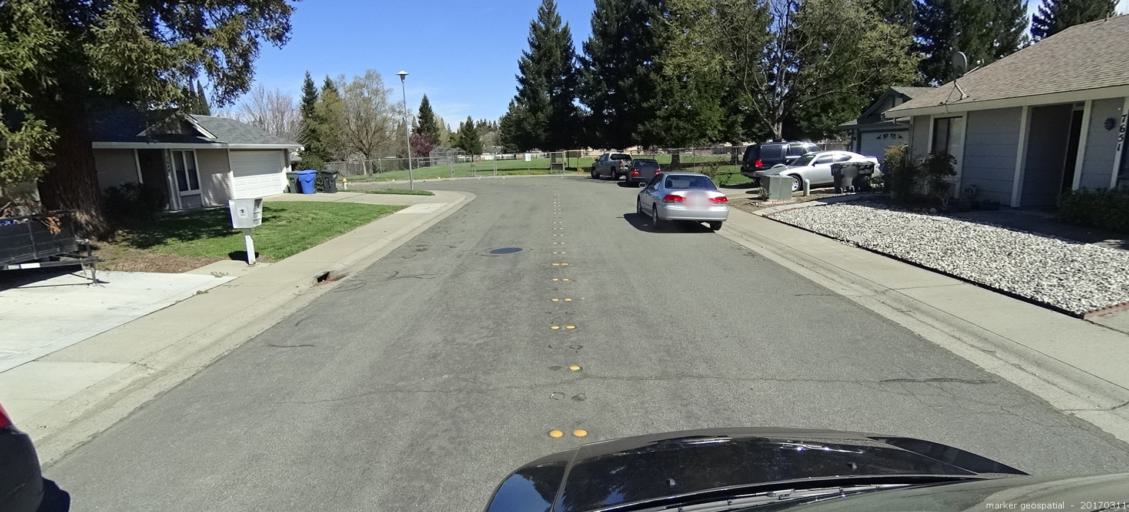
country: US
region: California
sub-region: Sacramento County
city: Parkway
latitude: 38.4817
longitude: -121.5392
